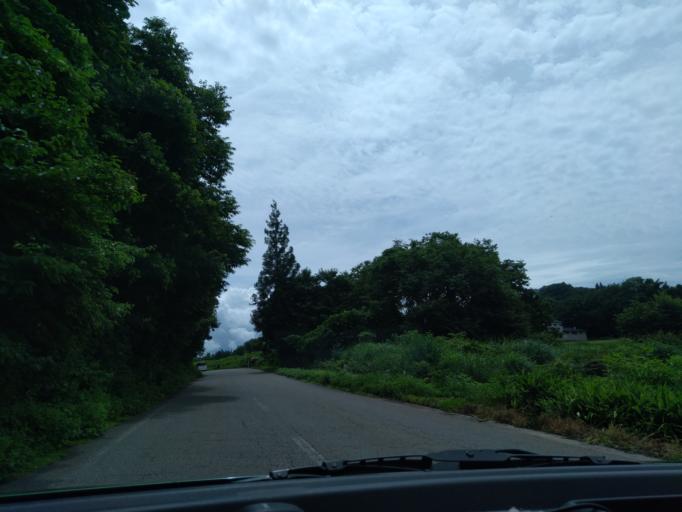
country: JP
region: Akita
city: Kakunodatemachi
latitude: 39.5806
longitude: 140.6253
